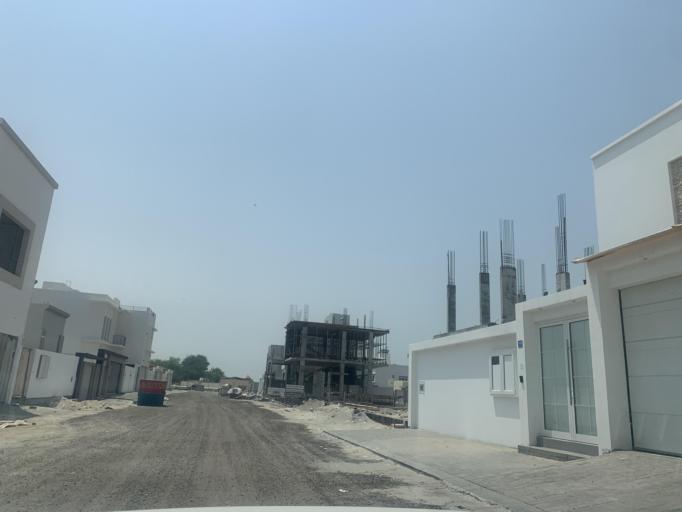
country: BH
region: Central Governorate
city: Madinat Hamad
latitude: 26.1443
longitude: 50.4664
